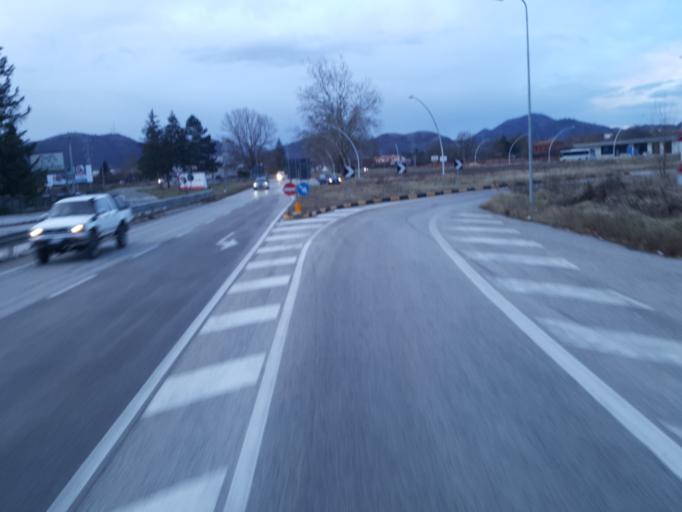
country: IT
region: Abruzzo
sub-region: Provincia dell' Aquila
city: Carsoli
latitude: 42.0816
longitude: 13.0595
